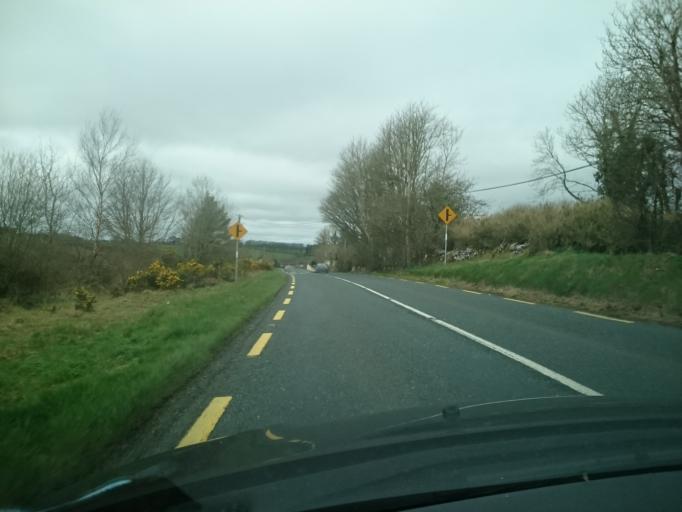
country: IE
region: Connaught
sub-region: Maigh Eo
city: Claremorris
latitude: 53.7730
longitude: -9.0629
